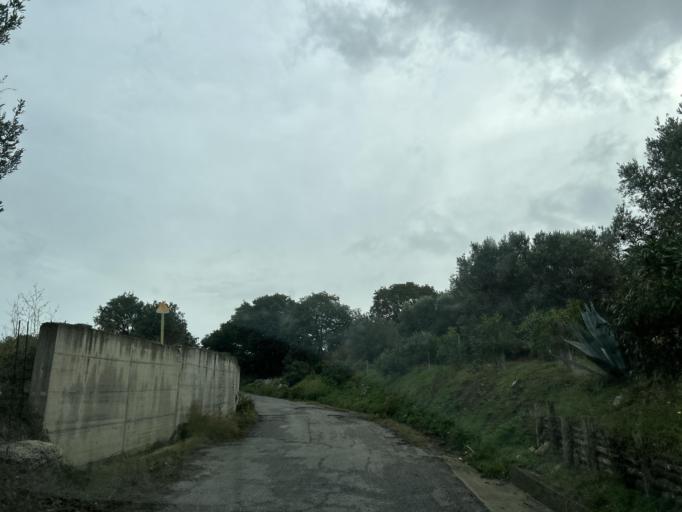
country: IT
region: Calabria
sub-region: Provincia di Catanzaro
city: Staletti
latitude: 38.7674
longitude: 16.5328
